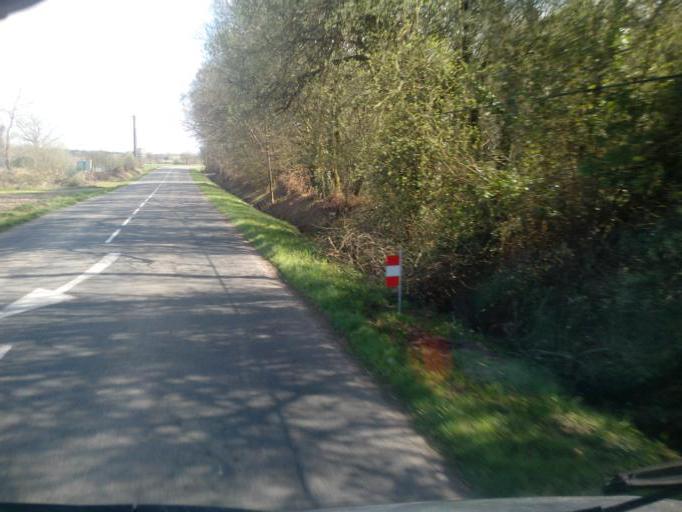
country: FR
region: Brittany
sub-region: Departement d'Ille-et-Vilaine
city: Paimpont
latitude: 48.0644
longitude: -2.1872
